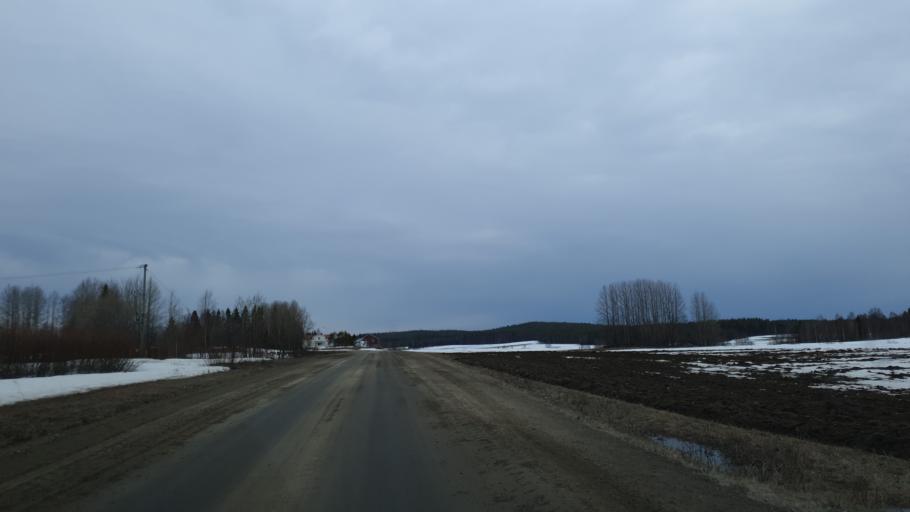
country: SE
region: Vaesterbotten
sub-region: Skelleftea Kommun
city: Burea
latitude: 64.3310
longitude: 21.1344
